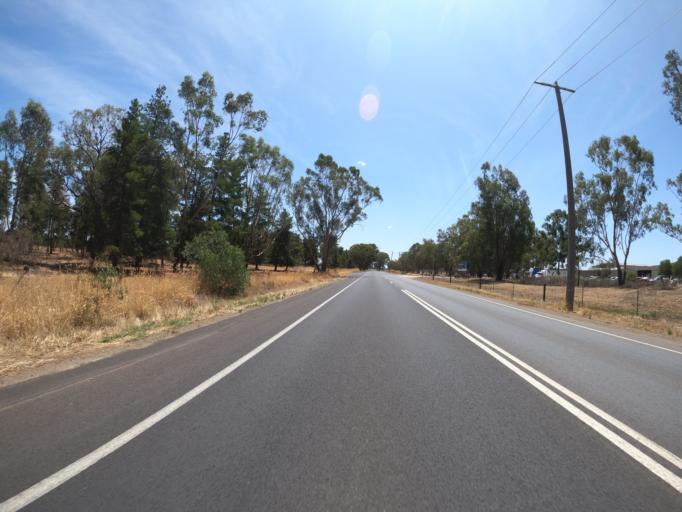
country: AU
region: Victoria
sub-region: Benalla
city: Benalla
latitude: -36.5273
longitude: 146.0392
